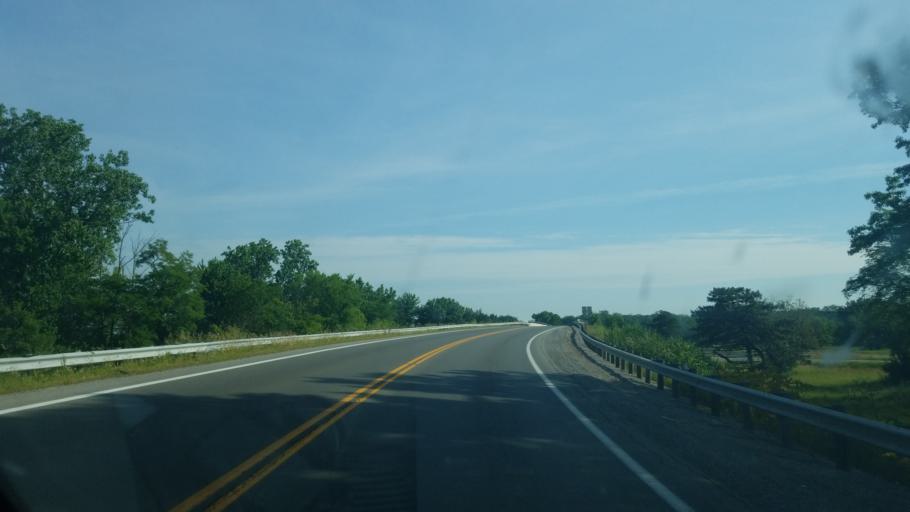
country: US
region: Ohio
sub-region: Hancock County
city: Findlay
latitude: 40.9922
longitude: -83.6517
